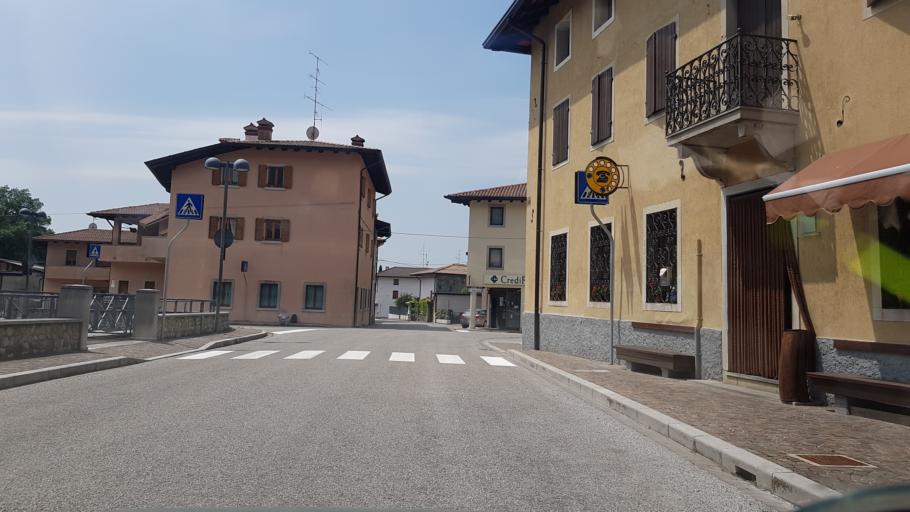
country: IT
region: Friuli Venezia Giulia
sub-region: Provincia di Udine
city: Torreano
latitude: 46.1314
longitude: 13.4335
